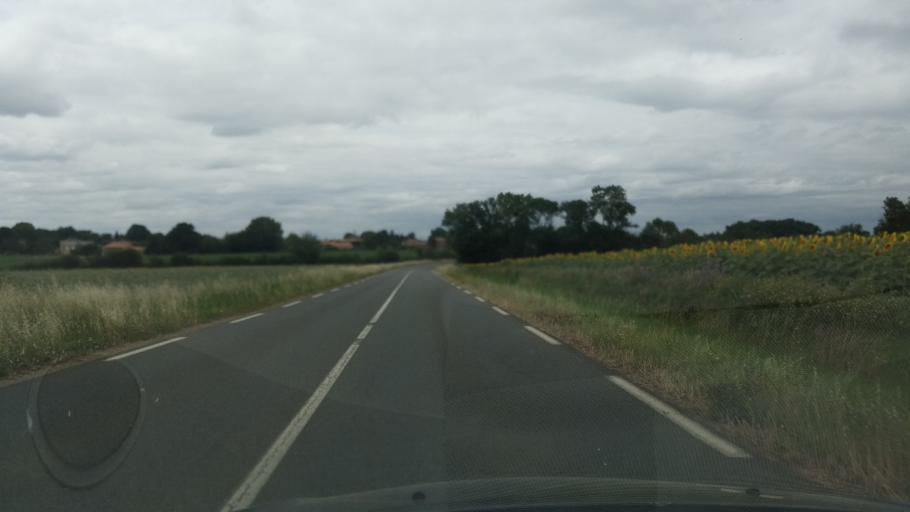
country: FR
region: Poitou-Charentes
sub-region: Departement de la Vienne
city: La Villedieu-du-Clain
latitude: 46.4376
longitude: 0.3720
